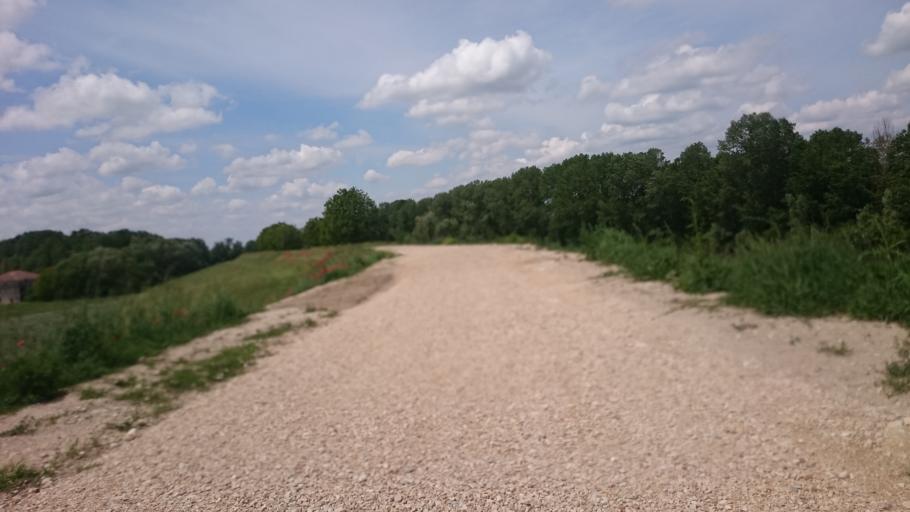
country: IT
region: Lombardy
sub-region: Provincia di Mantova
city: Roncoferraro
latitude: 45.0964
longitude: 10.9268
